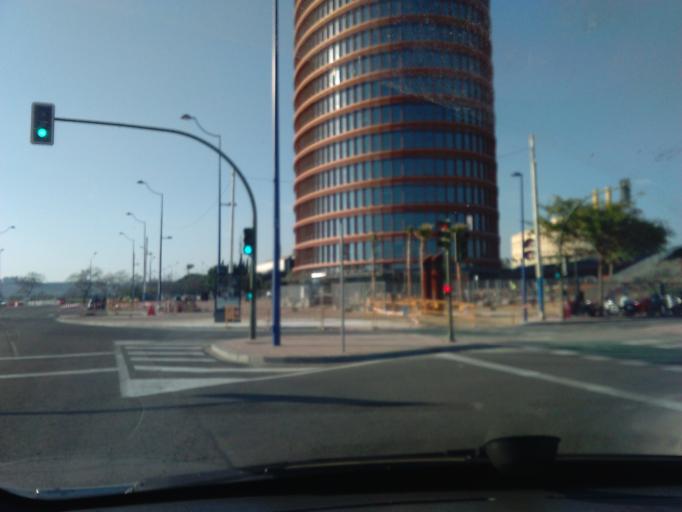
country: ES
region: Andalusia
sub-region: Provincia de Sevilla
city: Camas
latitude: 37.3907
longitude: -6.0094
